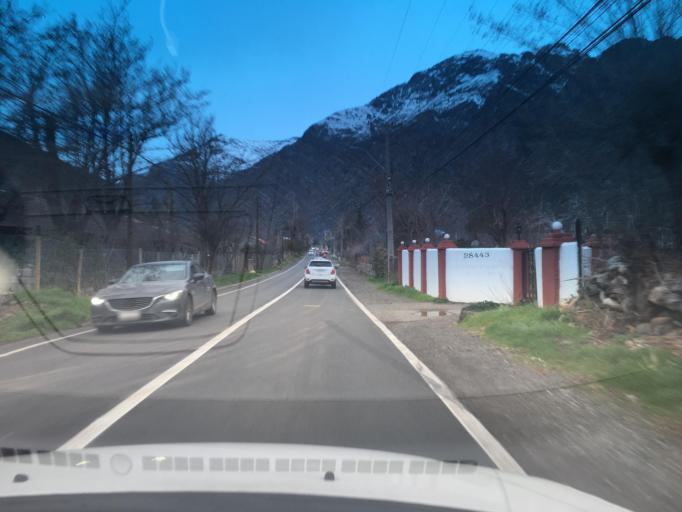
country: CL
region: Santiago Metropolitan
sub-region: Provincia de Cordillera
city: Puente Alto
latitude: -33.7102
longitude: -70.3326
